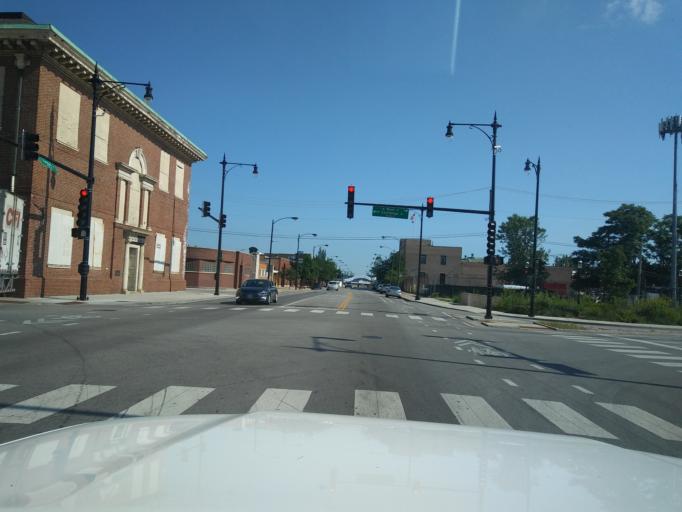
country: US
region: Illinois
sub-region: Cook County
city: Chicago
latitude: 41.8185
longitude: -87.6458
